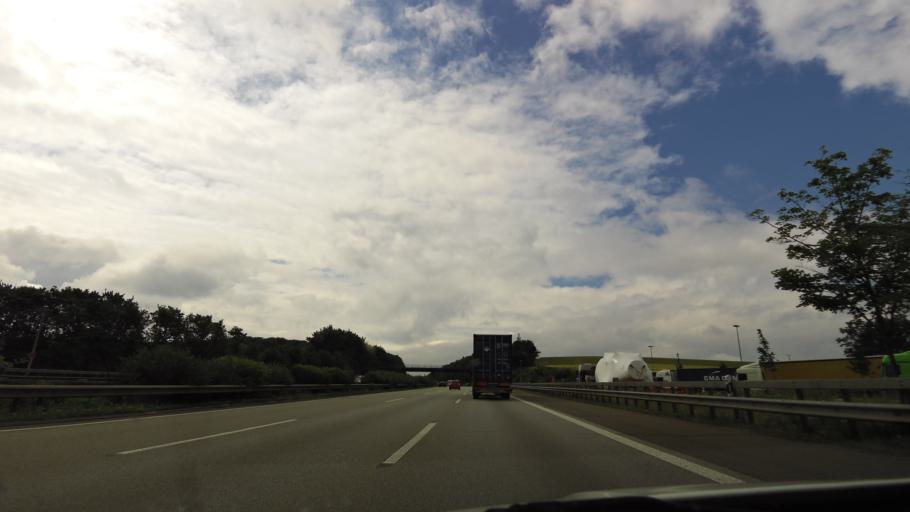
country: DE
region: Rheinland-Pfalz
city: Wehr
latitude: 50.4400
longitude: 7.2245
